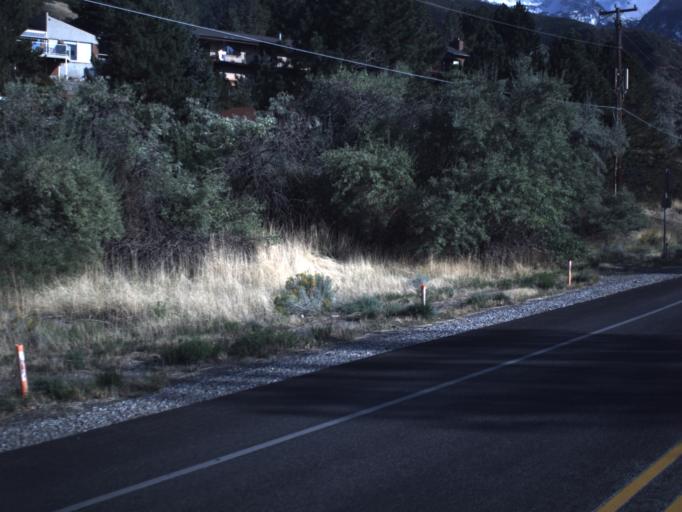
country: US
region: Utah
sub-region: Salt Lake County
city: Cottonwood Heights
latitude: 40.5976
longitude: -111.7979
